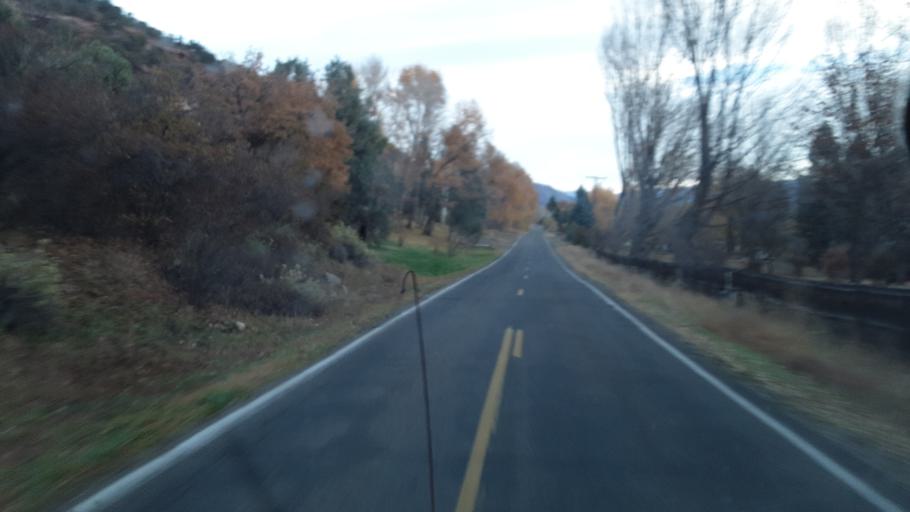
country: US
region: Colorado
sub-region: La Plata County
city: Durango
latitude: 37.3503
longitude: -107.8573
